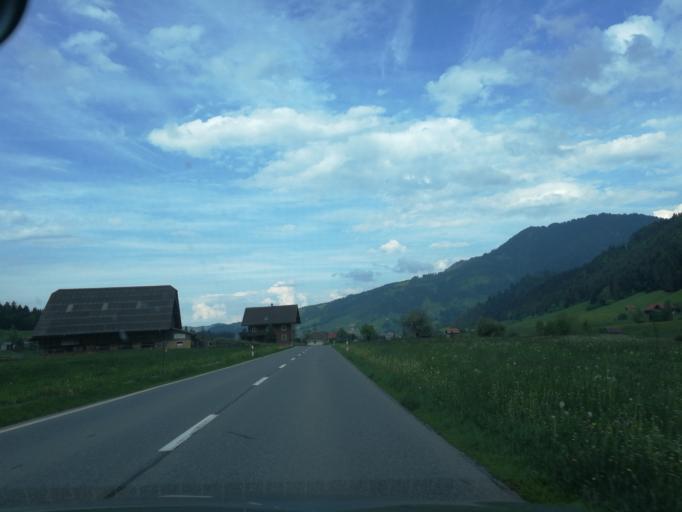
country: CH
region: Lucerne
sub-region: Entlebuch District
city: Escholzmatt
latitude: 46.9314
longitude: 7.9760
